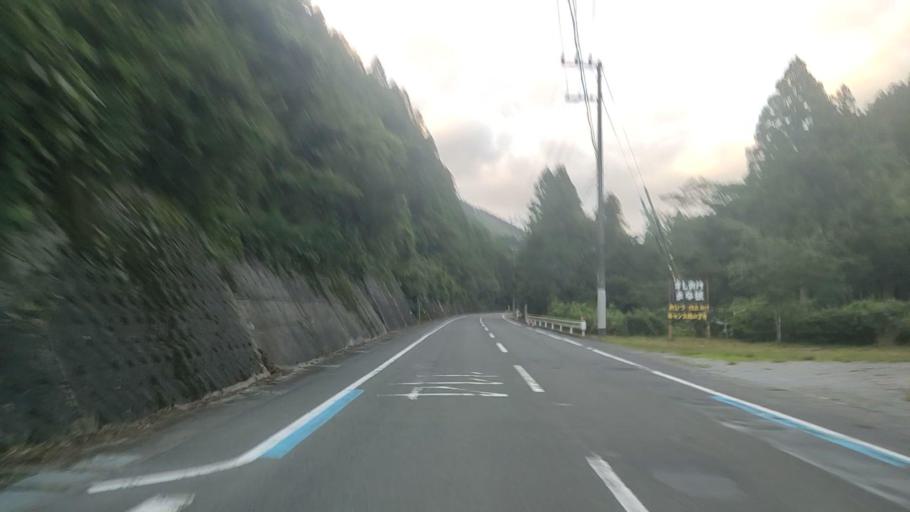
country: JP
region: Wakayama
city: Tanabe
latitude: 33.8281
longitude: 135.6400
